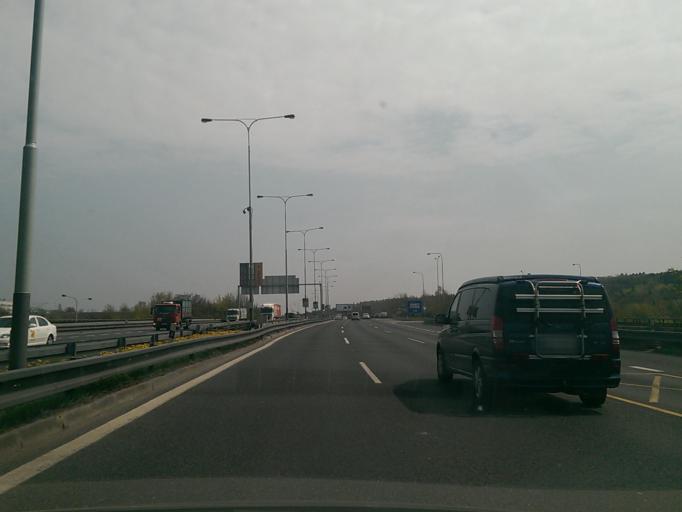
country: CZ
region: Praha
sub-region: Praha 4
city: Hodkovicky
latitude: 50.0379
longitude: 14.4565
